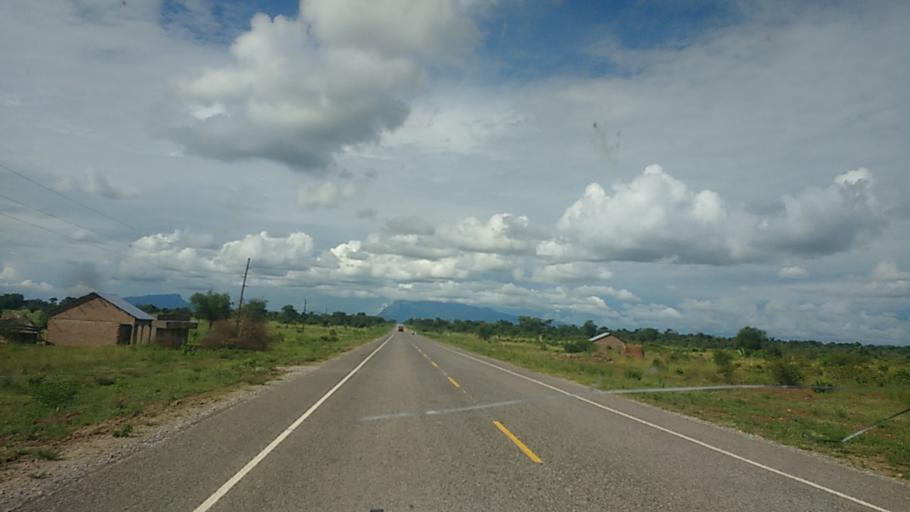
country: UG
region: Eastern Region
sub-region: Katakwi District
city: Katakwi
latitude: 1.9263
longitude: 34.0579
